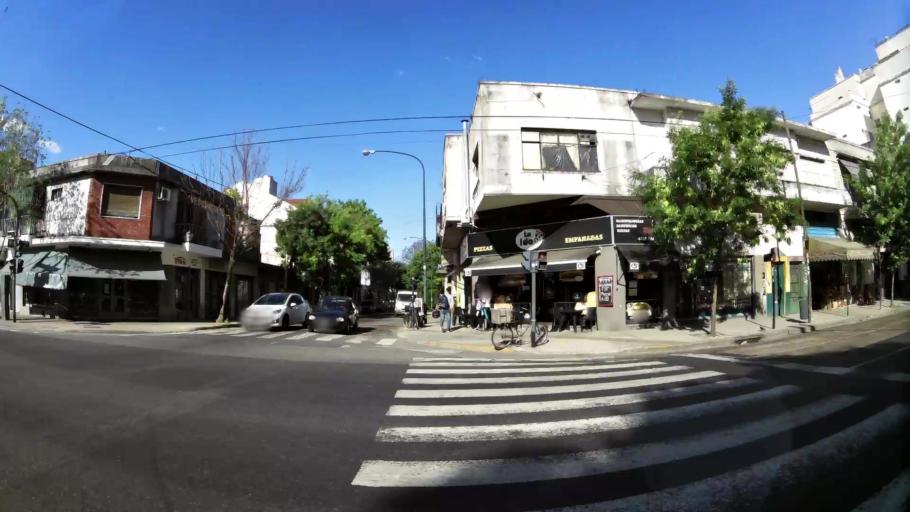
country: AR
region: Buenos Aires F.D.
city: Villa Santa Rita
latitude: -34.6233
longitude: -58.4730
